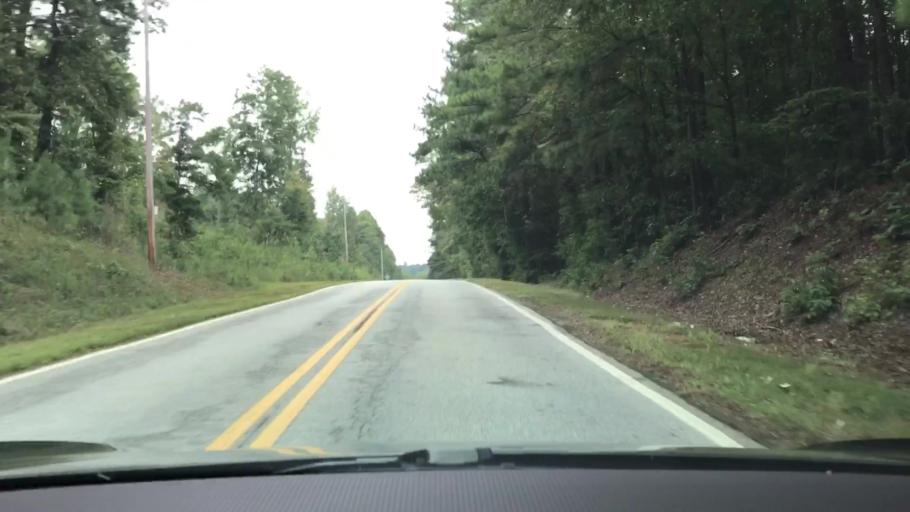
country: US
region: Georgia
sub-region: Barrow County
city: Auburn
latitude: 34.0522
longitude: -83.8198
